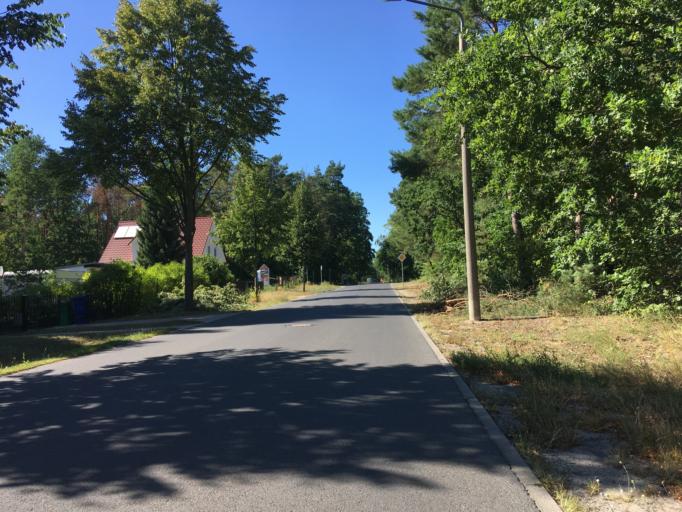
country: DE
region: Brandenburg
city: Schulzendorf
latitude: 52.3504
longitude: 13.5965
